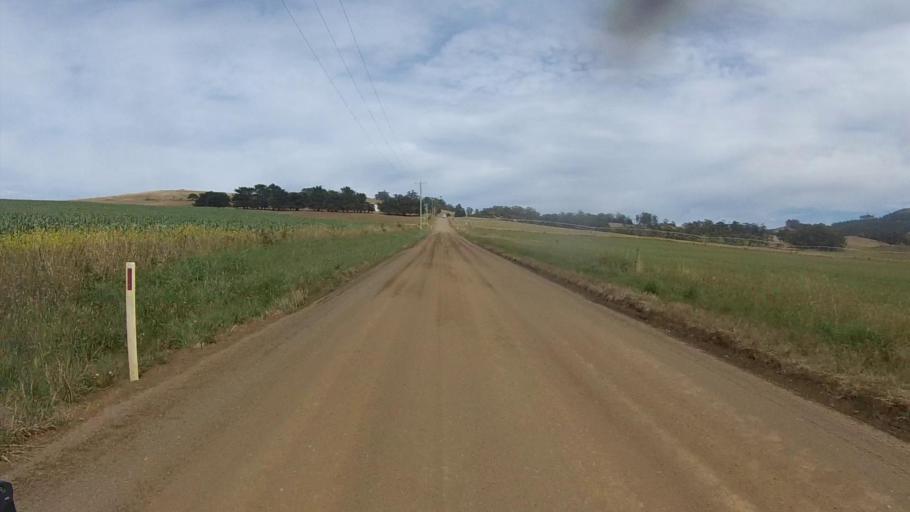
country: AU
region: Tasmania
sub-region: Sorell
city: Sorell
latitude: -42.8213
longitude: 147.8517
